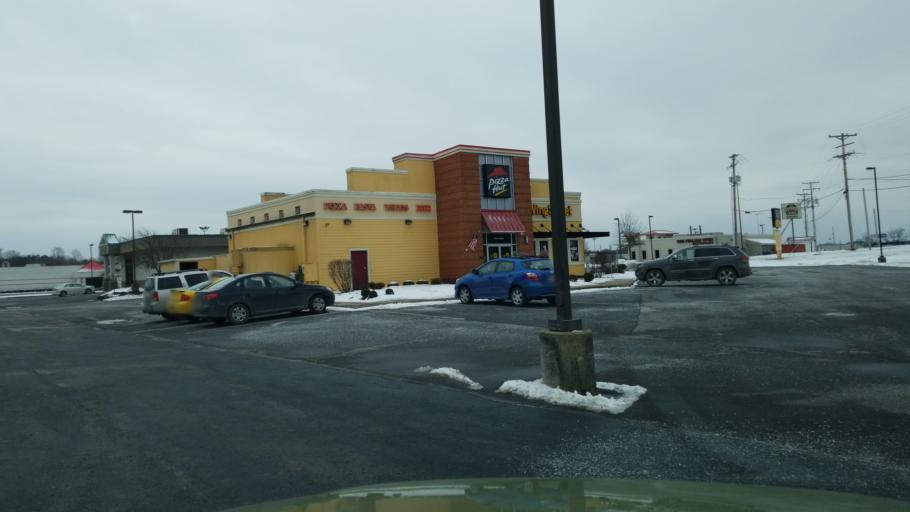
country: US
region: Pennsylvania
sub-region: Clearfield County
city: DuBois
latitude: 41.1220
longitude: -78.7233
